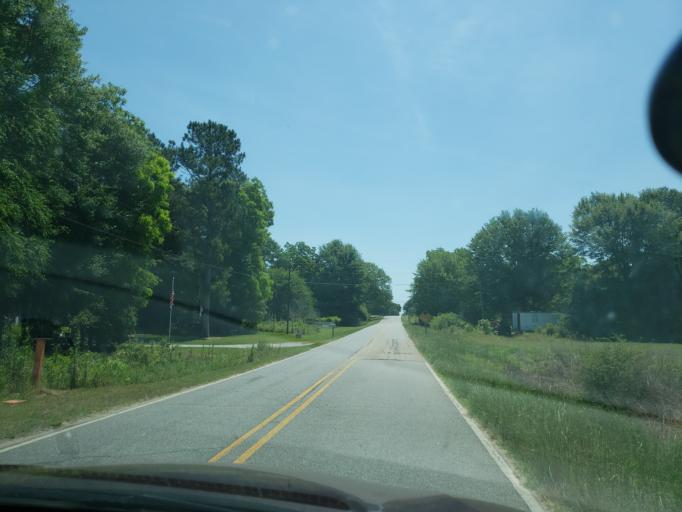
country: US
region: Alabama
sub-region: Elmore County
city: Tallassee
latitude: 32.5812
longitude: -85.7915
